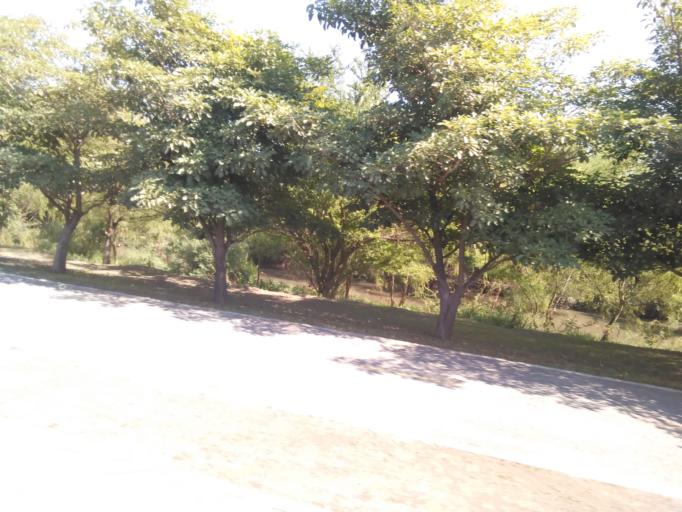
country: MX
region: Nayarit
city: Tepic
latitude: 21.4817
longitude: -104.8514
